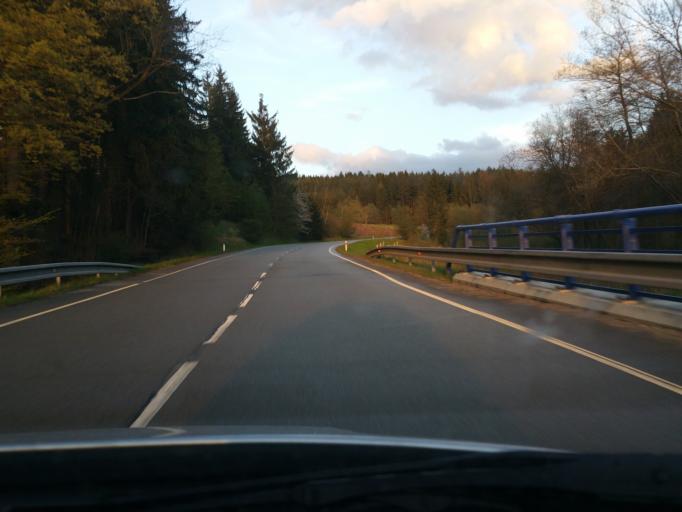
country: CZ
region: South Moravian
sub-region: Okres Blansko
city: Boskovice
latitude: 49.4644
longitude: 16.7281
